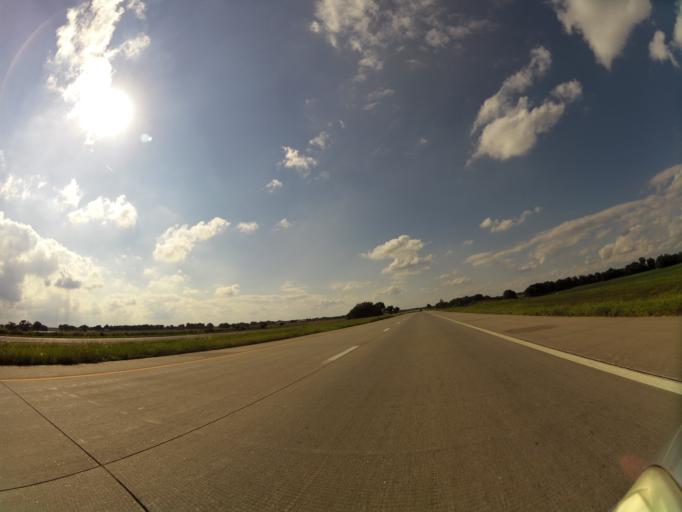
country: US
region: Kansas
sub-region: Sedgwick County
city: Colwich
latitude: 37.8626
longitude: -97.6182
